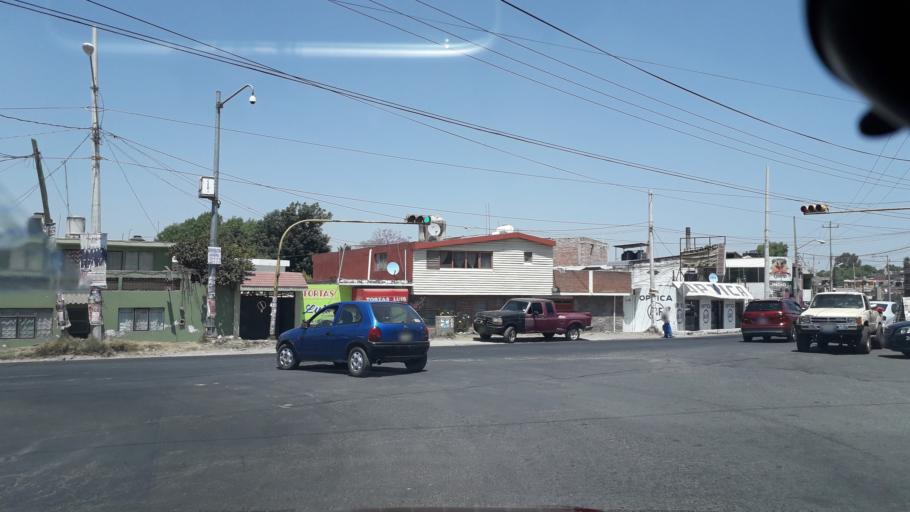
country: MX
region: Puebla
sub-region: Cuautlancingo
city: Sanctorum
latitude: 19.1008
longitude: -98.2286
